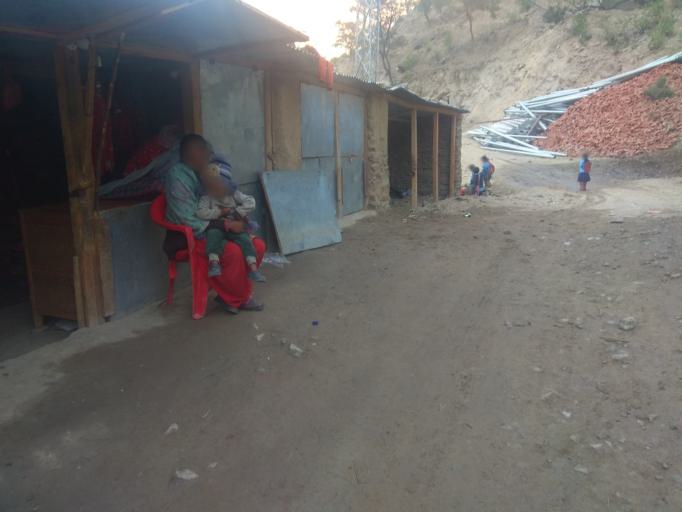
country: NP
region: Mid Western
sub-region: Bheri Zone
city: Dailekh
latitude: 29.2714
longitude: 81.7137
